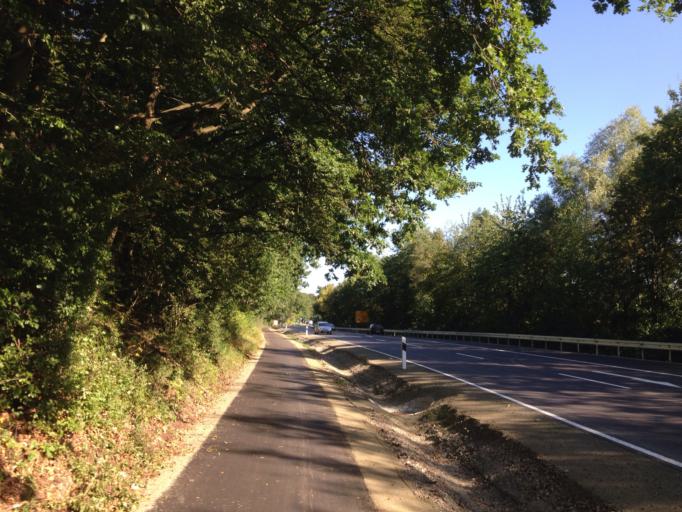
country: DE
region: Hesse
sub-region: Regierungsbezirk Giessen
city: Giessen
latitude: 50.5520
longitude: 8.7190
